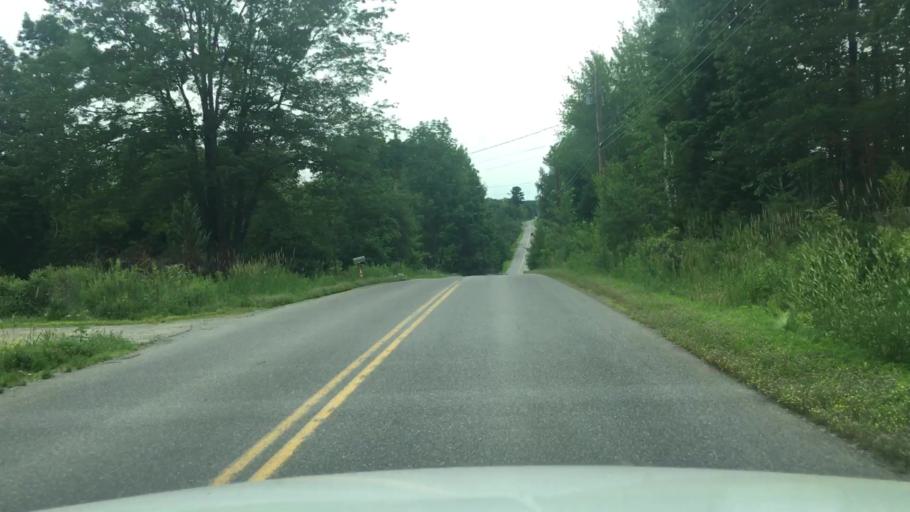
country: US
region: Maine
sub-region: Kennebec County
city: Clinton
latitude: 44.5820
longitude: -69.4942
